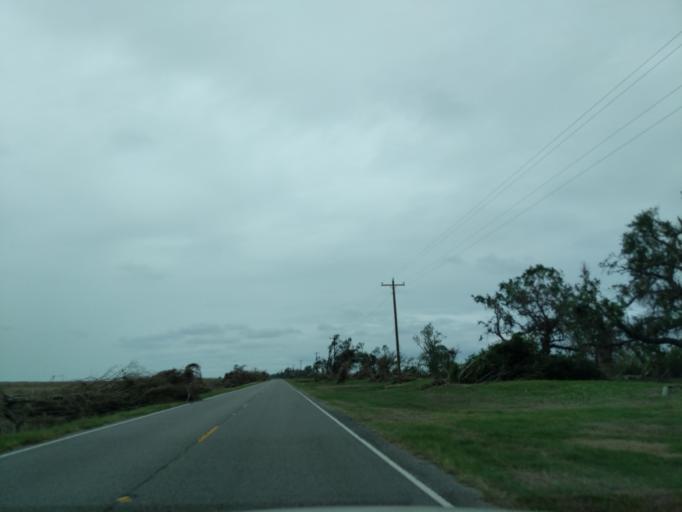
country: US
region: Louisiana
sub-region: Cameron Parish
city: Cameron
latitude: 29.7865
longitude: -93.1248
